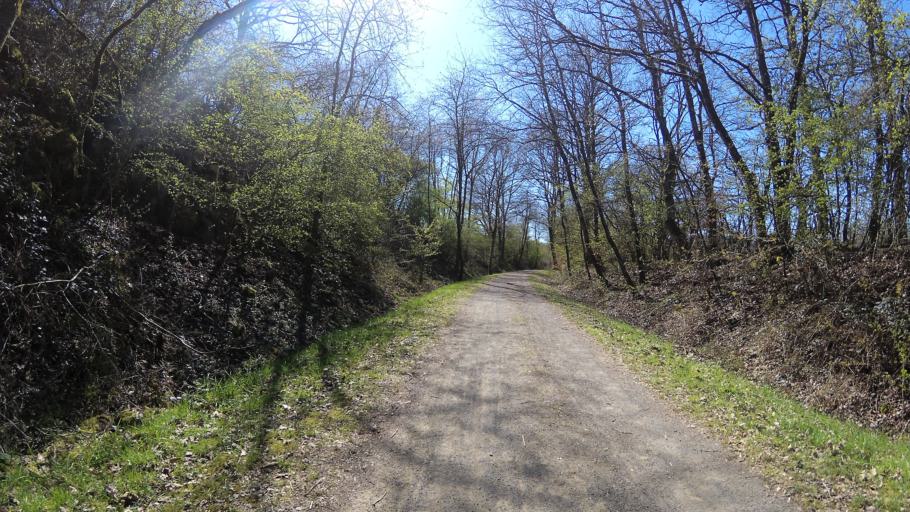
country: DE
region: Rheinland-Pfalz
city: Pfeffelbach
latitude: 49.5361
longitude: 7.3298
